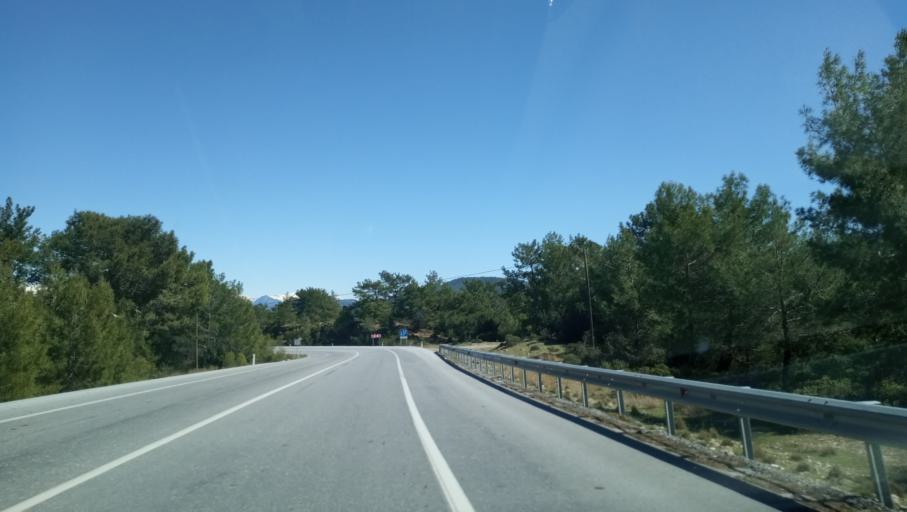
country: TR
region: Antalya
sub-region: Alanya
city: Okurcalar
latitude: 36.7730
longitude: 31.6806
